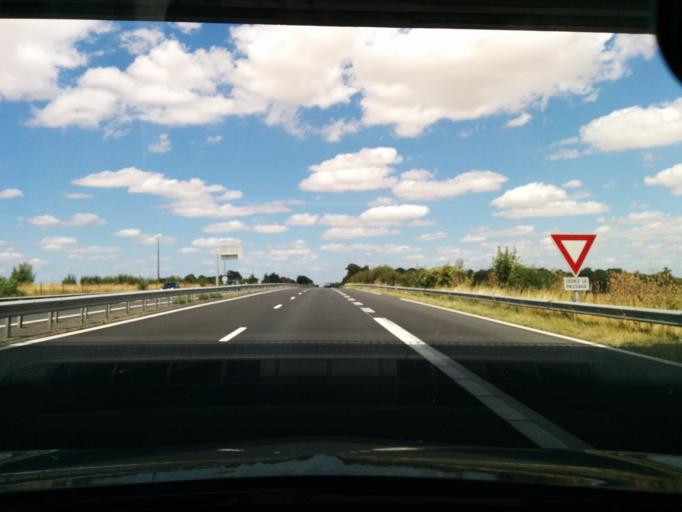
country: FR
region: Centre
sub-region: Departement de l'Indre
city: Montierchaume
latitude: 46.9519
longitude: 1.7558
